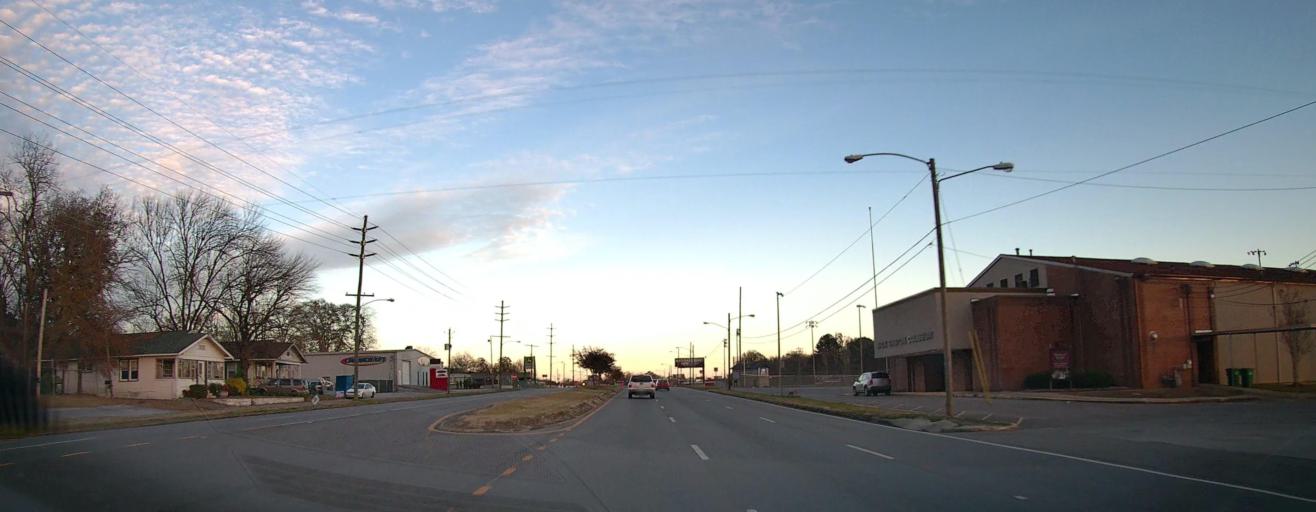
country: US
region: Alabama
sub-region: Etowah County
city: Gadsden
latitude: 34.0232
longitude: -86.0275
